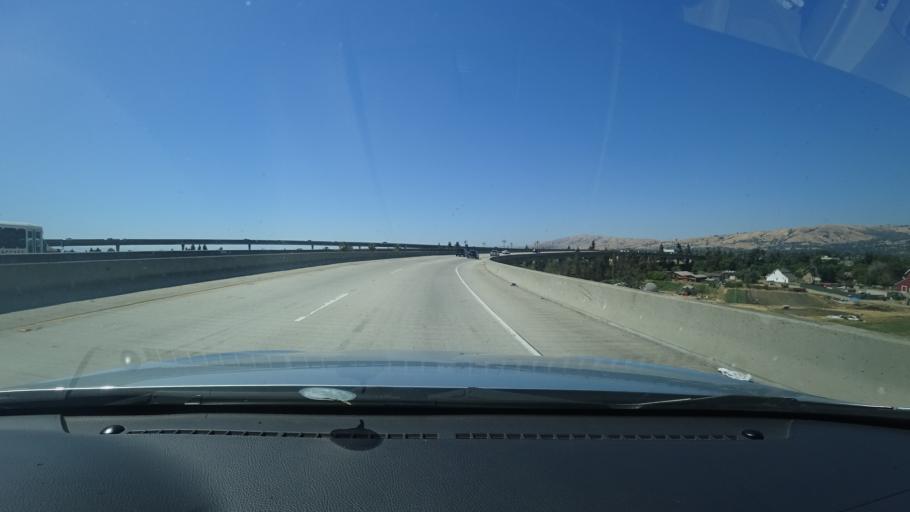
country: US
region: California
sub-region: Santa Clara County
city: Alum Rock
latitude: 37.3380
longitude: -121.8488
